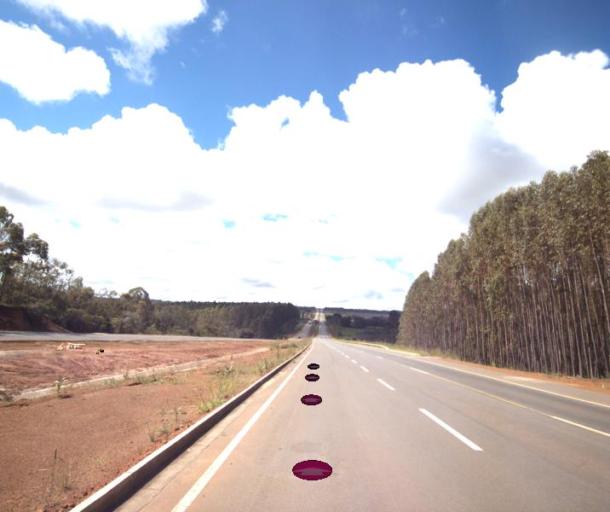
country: BR
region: Goias
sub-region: Anapolis
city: Anapolis
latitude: -16.2058
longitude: -49.0211
